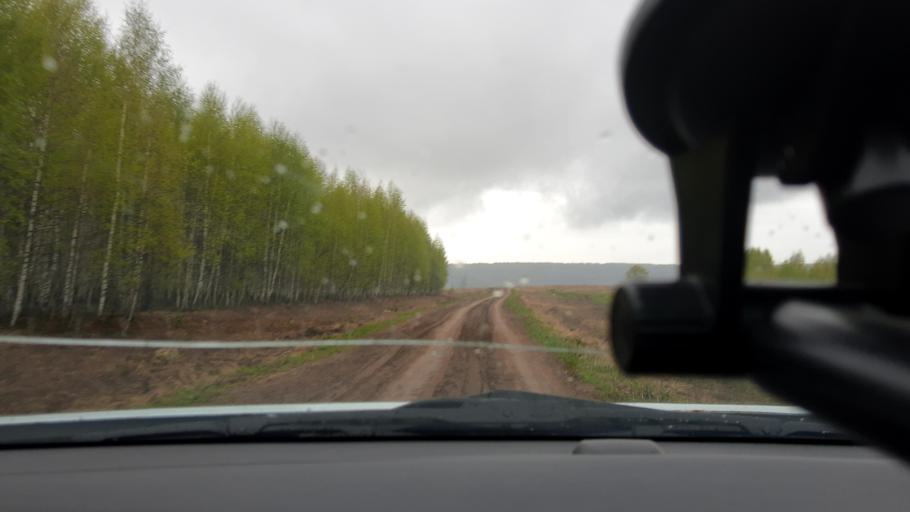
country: RU
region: Bashkortostan
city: Pavlovka
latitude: 55.4252
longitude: 56.3337
